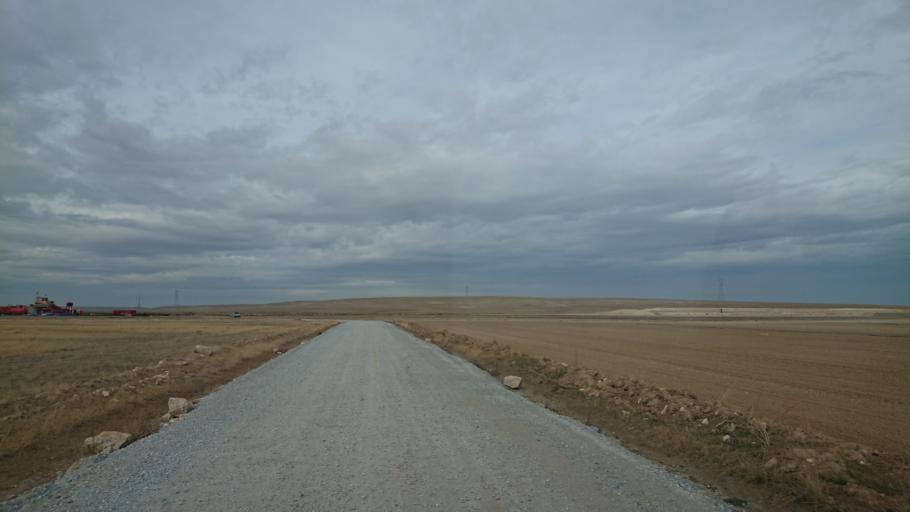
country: TR
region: Aksaray
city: Sultanhani
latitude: 38.1329
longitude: 33.5519
